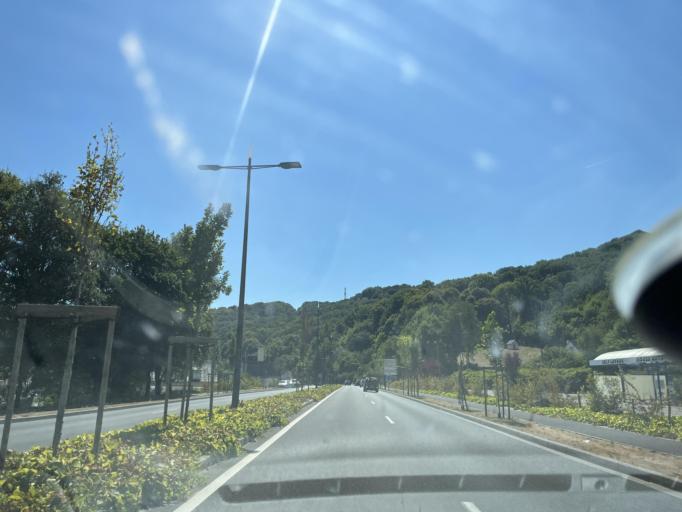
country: FR
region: Haute-Normandie
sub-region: Departement de la Seine-Maritime
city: Lillebonne
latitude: 49.5214
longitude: 0.5291
